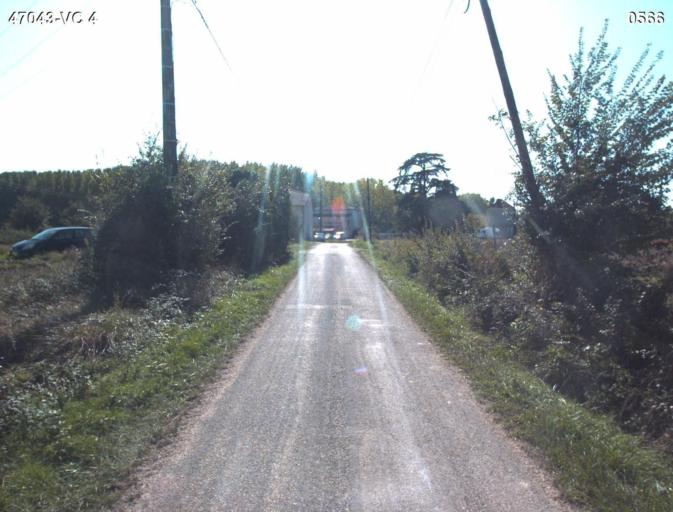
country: FR
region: Aquitaine
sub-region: Departement du Lot-et-Garonne
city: Buzet-sur-Baise
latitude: 44.2622
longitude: 0.3102
